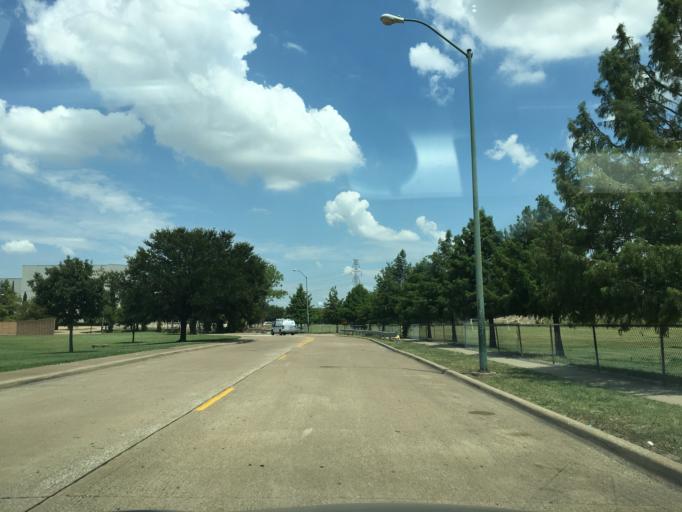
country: US
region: Texas
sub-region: Dallas County
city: Garland
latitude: 32.8678
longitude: -96.6743
